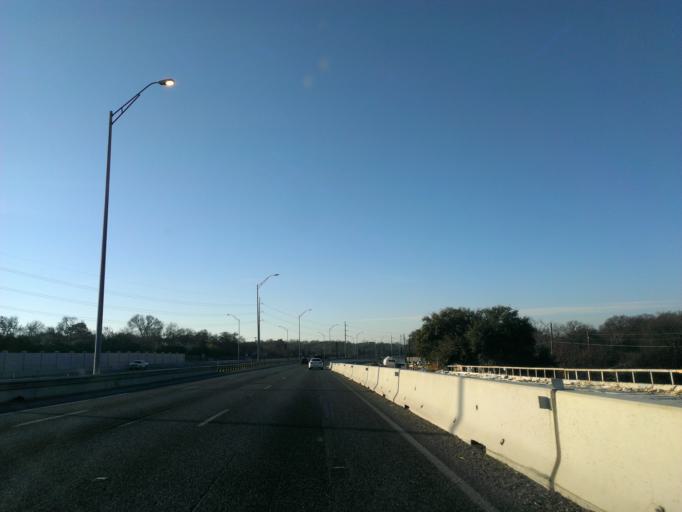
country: US
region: Texas
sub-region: Travis County
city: Austin
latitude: 30.3009
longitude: -97.7586
